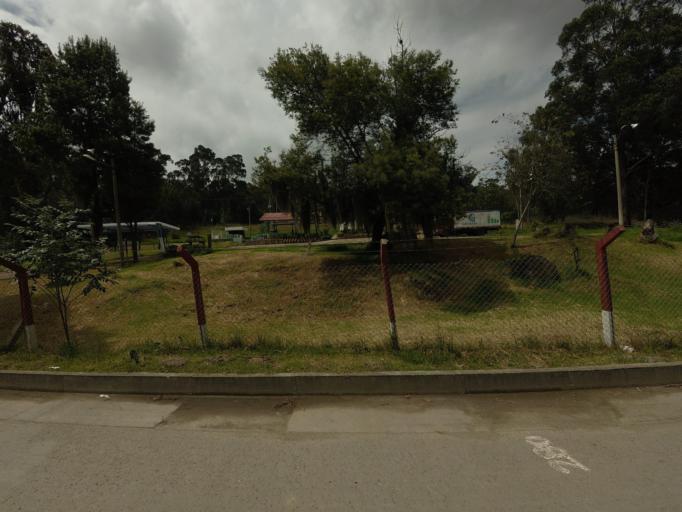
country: CO
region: Boyaca
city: Sogamoso
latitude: 5.7330
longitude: -72.9593
